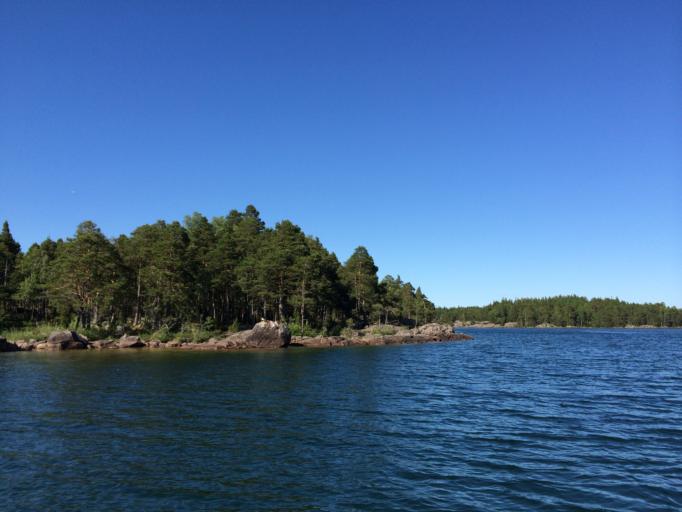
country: SE
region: OErebro
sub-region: Askersunds Kommun
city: Askersund
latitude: 58.7519
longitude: 14.8437
